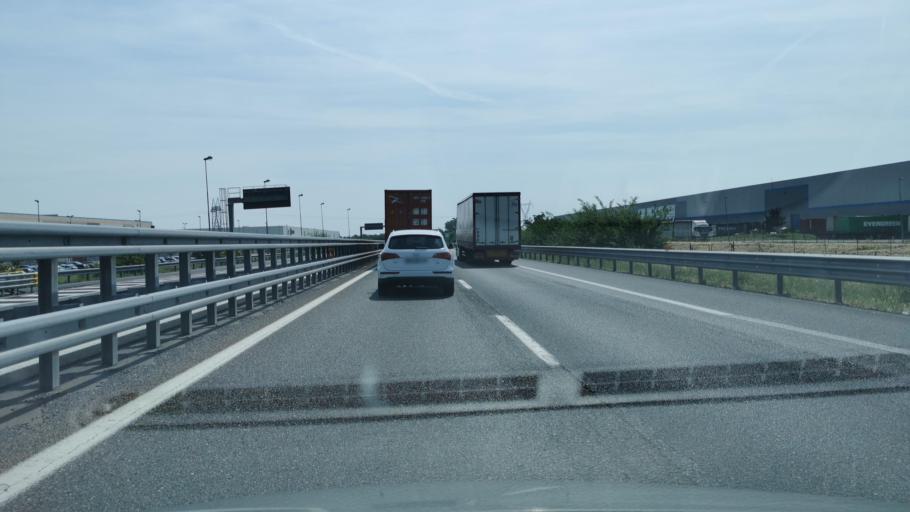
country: IT
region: Emilia-Romagna
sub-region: Provincia di Piacenza
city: Castel San Giovanni
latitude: 45.0745
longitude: 9.4533
